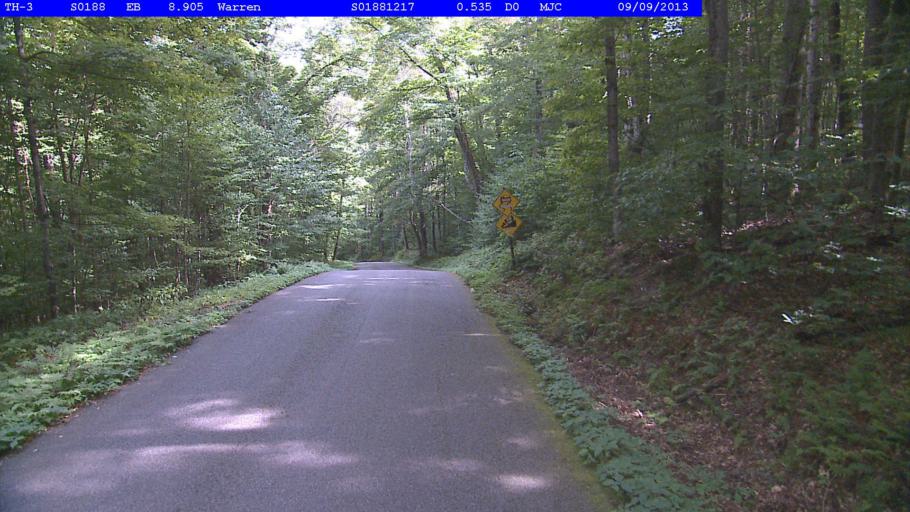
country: US
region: Vermont
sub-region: Addison County
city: Bristol
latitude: 44.0922
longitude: -72.9141
